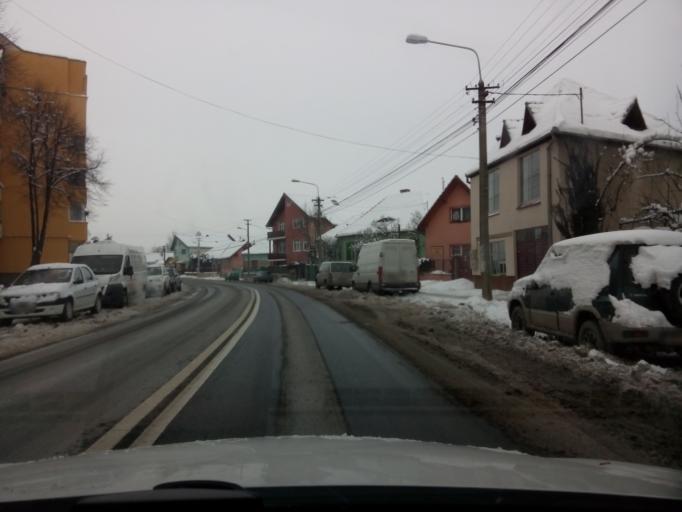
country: RO
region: Sibiu
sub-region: Municipiul Sibiu
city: Sibiu
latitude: 45.8070
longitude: 24.1518
